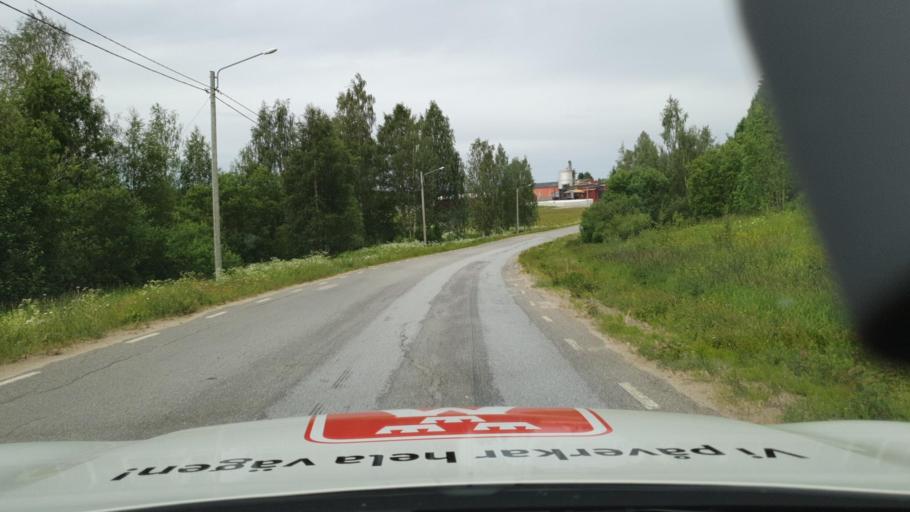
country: SE
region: Vaesterbotten
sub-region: Robertsfors Kommun
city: Robertsfors
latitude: 64.2576
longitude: 20.6489
